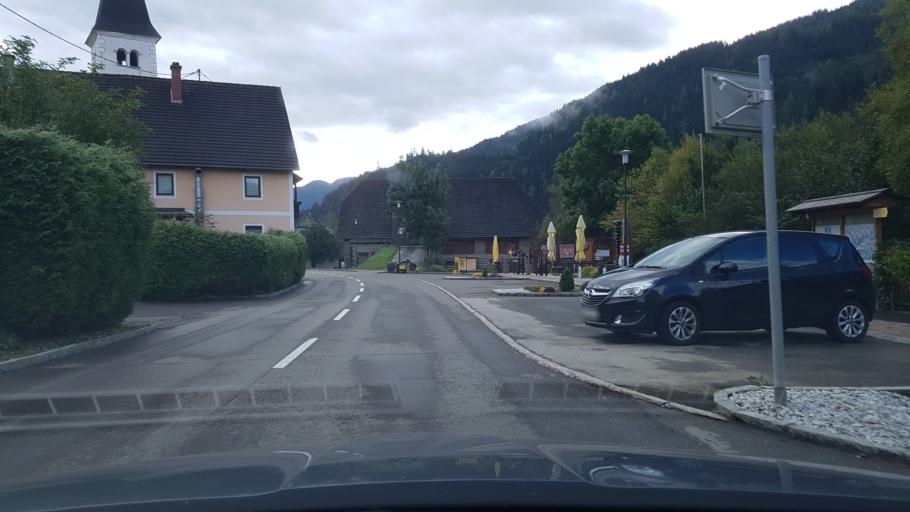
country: AT
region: Styria
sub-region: Politischer Bezirk Murau
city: Winklern bei Oberwolz
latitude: 47.1657
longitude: 14.2411
